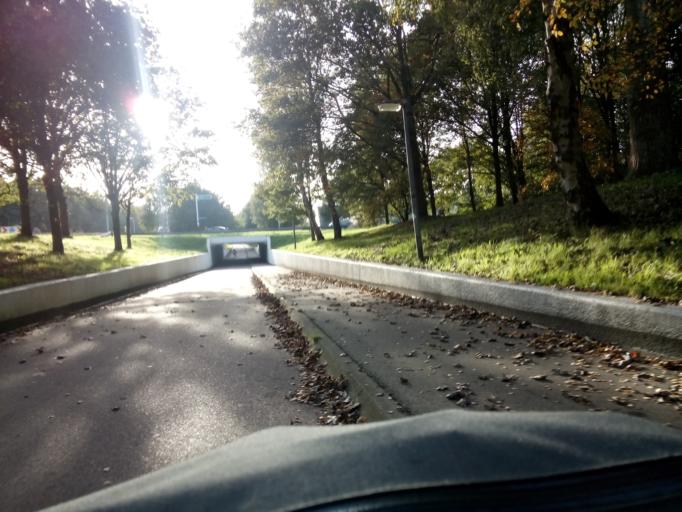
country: NL
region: Drenthe
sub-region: Gemeente Assen
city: Assen
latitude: 52.9846
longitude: 6.5396
